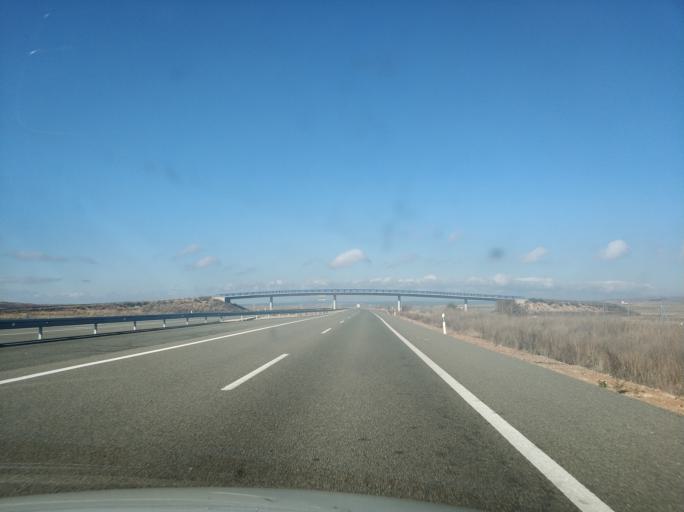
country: ES
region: Castille and Leon
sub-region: Provincia de Soria
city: Adradas
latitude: 41.3899
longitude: -2.4705
